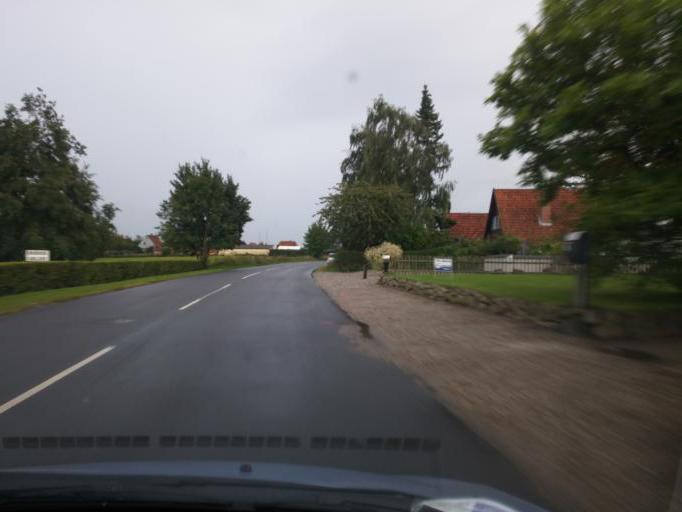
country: DK
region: South Denmark
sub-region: Odense Kommune
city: Bellinge
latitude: 55.3947
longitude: 10.3081
